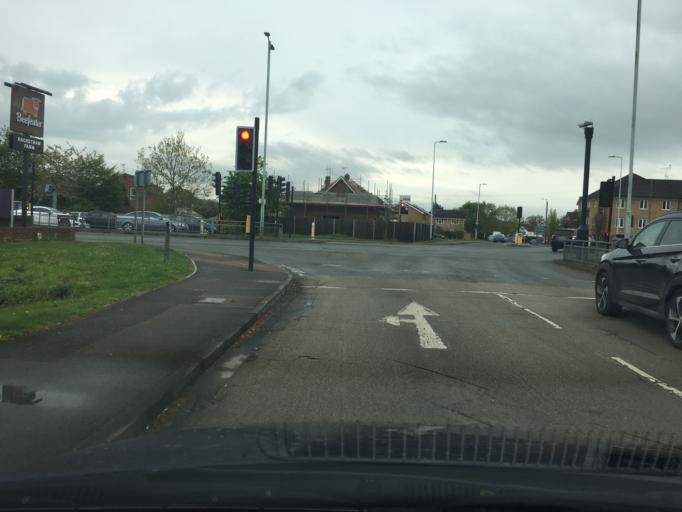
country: GB
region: England
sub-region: Bracknell Forest
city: Sandhurst
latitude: 51.3453
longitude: -0.7862
